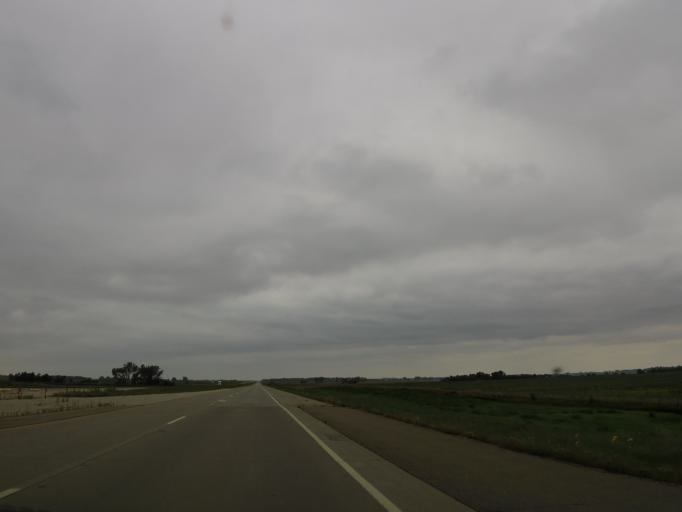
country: US
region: South Dakota
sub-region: Roberts County
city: Sisseton
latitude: 45.5579
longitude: -96.9892
